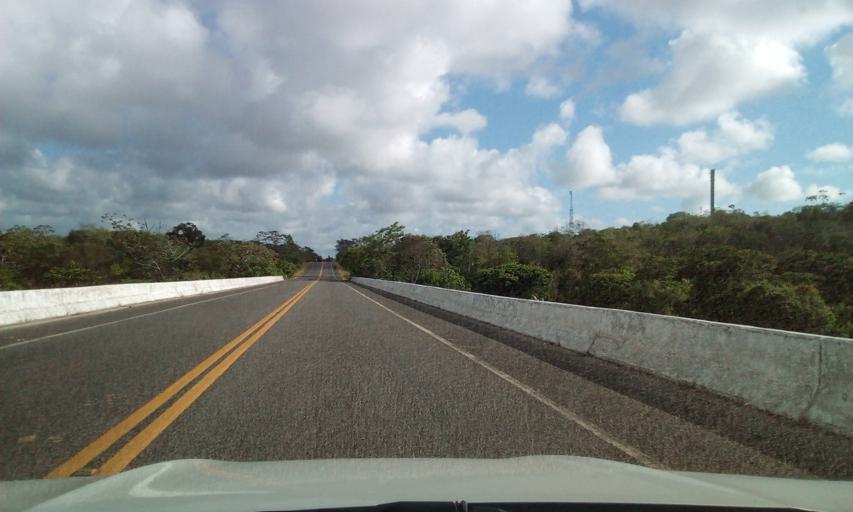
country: BR
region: Bahia
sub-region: Conde
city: Conde
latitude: -11.8070
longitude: -37.6310
